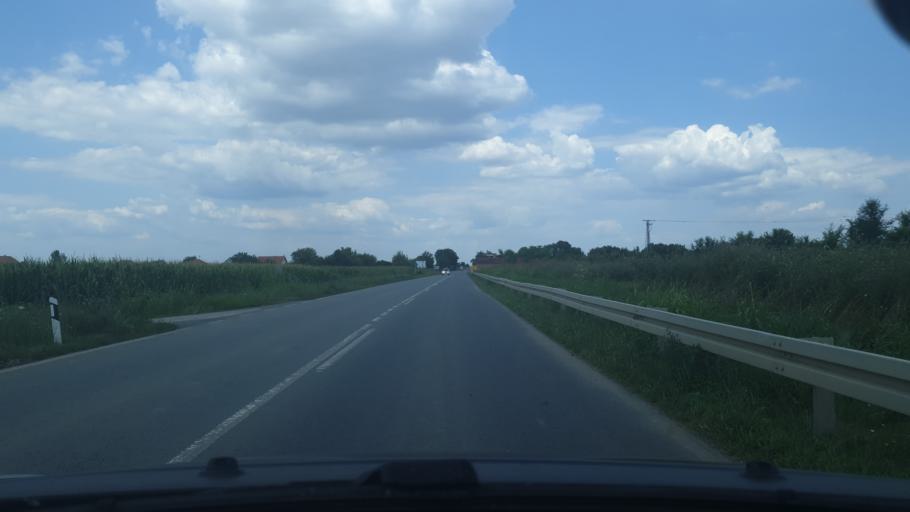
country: RS
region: Autonomna Pokrajina Vojvodina
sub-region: Sremski Okrug
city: Pecinci
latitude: 44.9044
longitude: 19.9565
